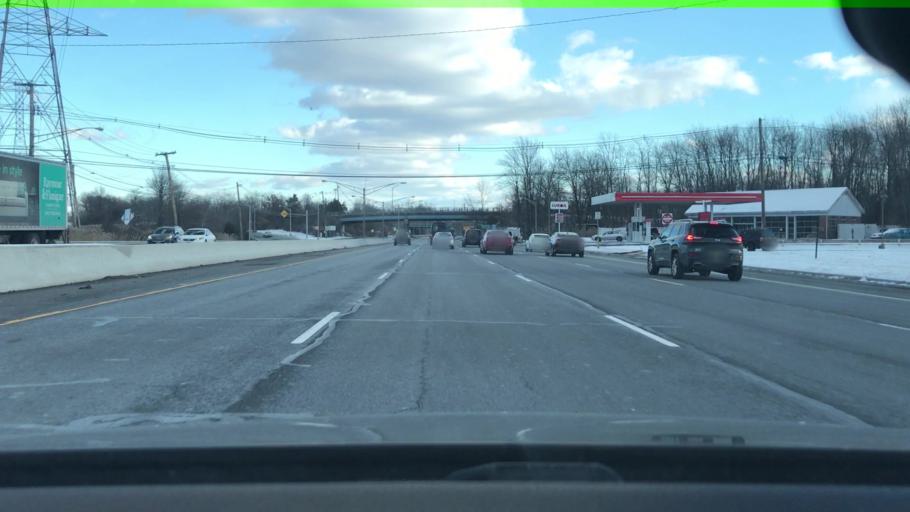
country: US
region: New Jersey
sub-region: Morris County
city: Parsippany
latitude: 40.8347
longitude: -74.4430
